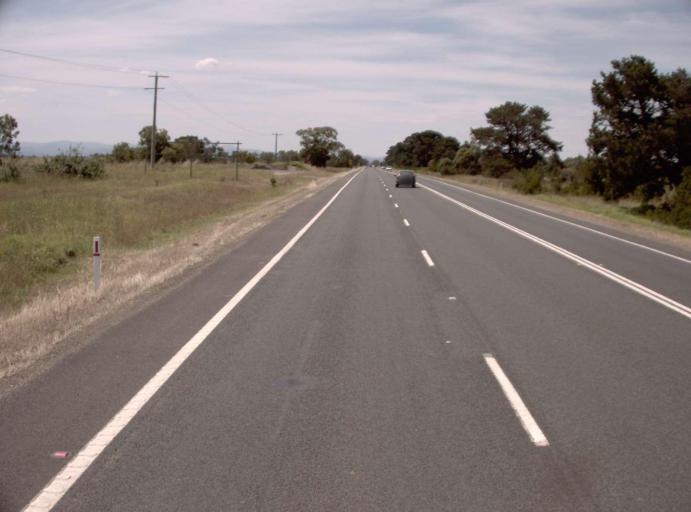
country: AU
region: Victoria
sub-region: Wellington
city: Sale
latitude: -38.0214
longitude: 147.0599
